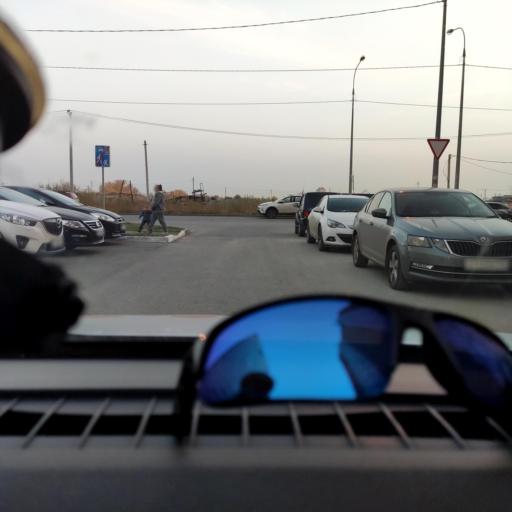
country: RU
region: Samara
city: Samara
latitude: 53.1468
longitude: 50.0775
